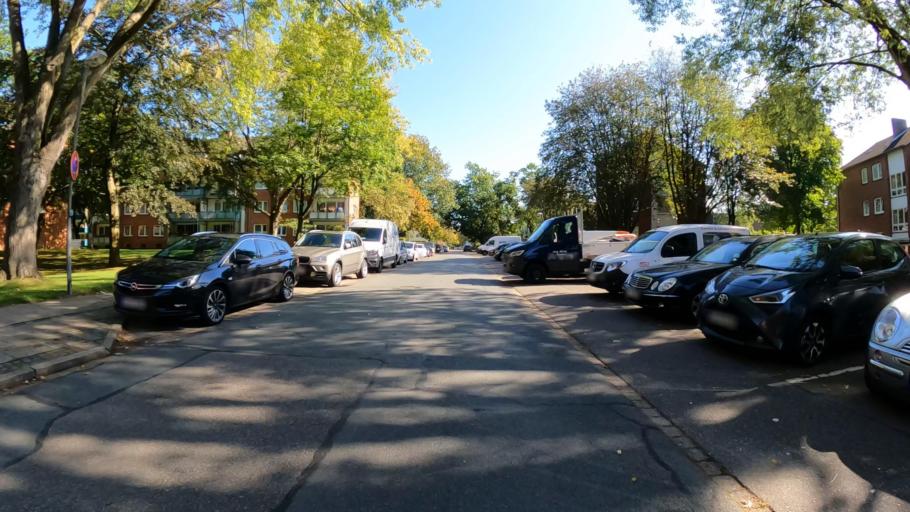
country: DE
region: Schleswig-Holstein
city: Ahrensburg
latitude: 53.6761
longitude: 10.2305
